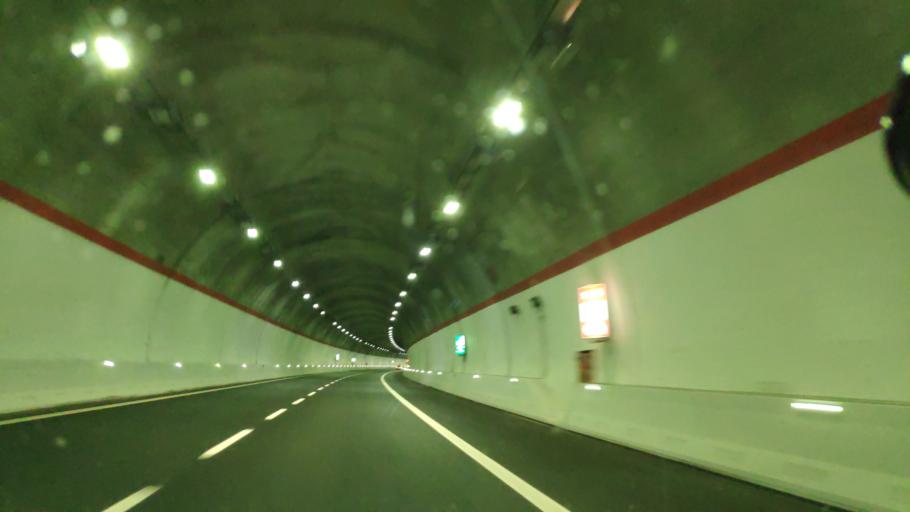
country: IT
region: Campania
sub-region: Provincia di Salerno
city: Casalbuono
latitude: 40.2270
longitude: 15.6703
